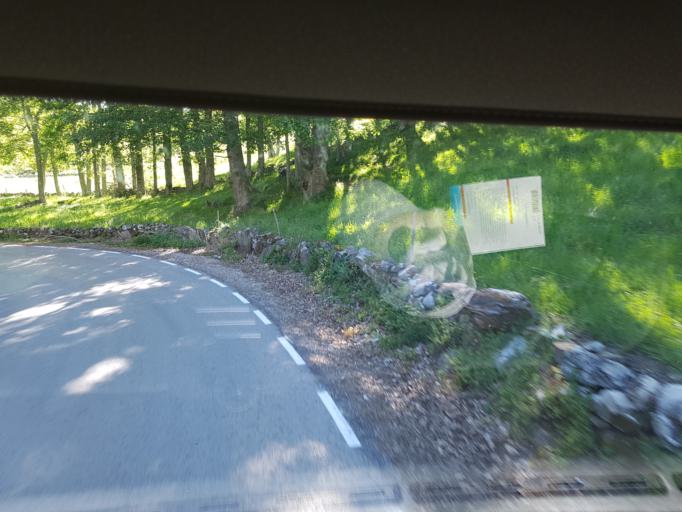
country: ES
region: Castille and Leon
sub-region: Provincia de Burgos
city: Espinosa de los Monteros
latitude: 43.1210
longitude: -3.5791
